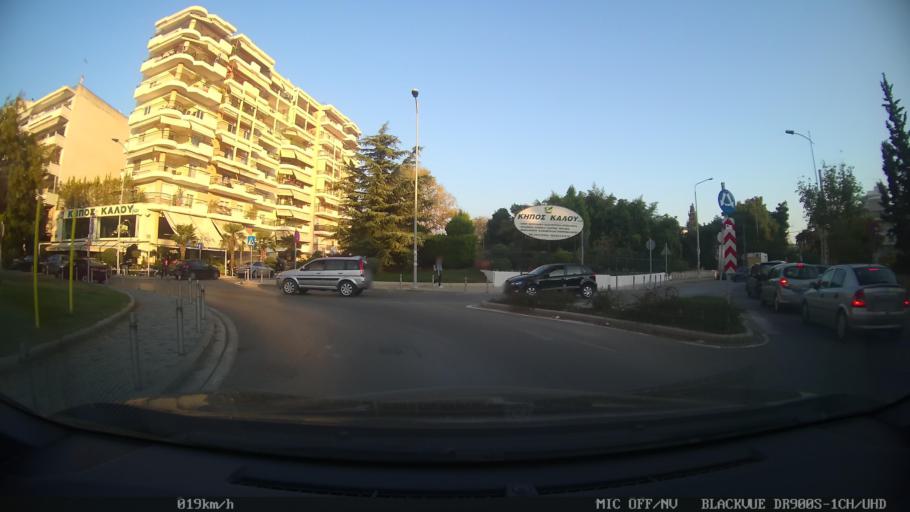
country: GR
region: Central Macedonia
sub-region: Nomos Thessalonikis
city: Triandria
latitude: 40.6046
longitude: 22.9740
